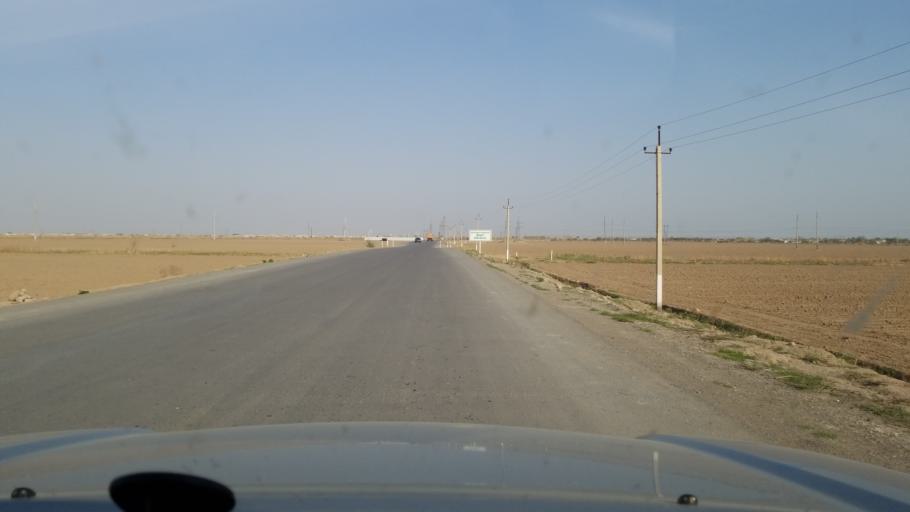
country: AF
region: Jowzjan
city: Khamyab
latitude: 37.6065
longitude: 65.7348
